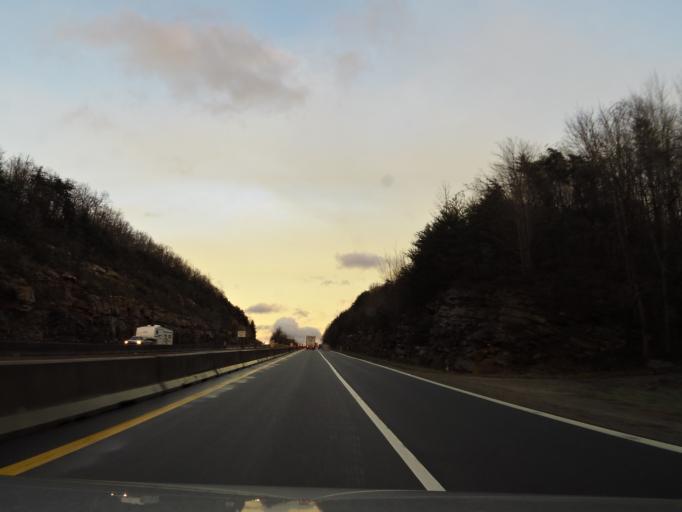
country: US
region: Tennessee
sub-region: Campbell County
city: Jacksboro
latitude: 36.4372
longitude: -84.2895
